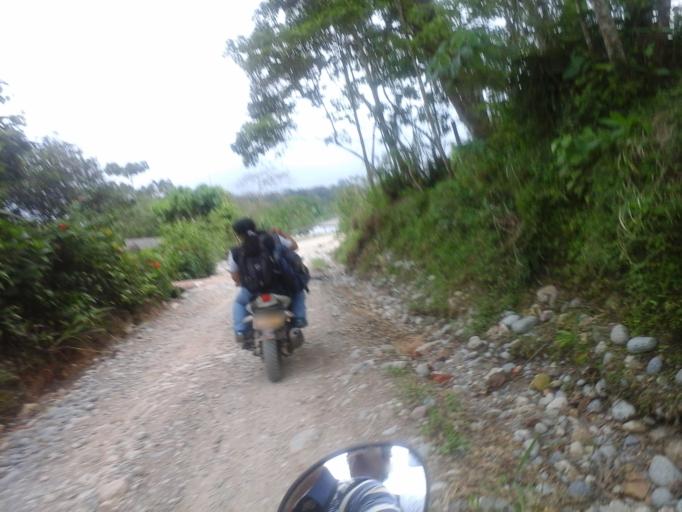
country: CO
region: Putumayo
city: Mocoa
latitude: 1.1829
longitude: -76.6725
